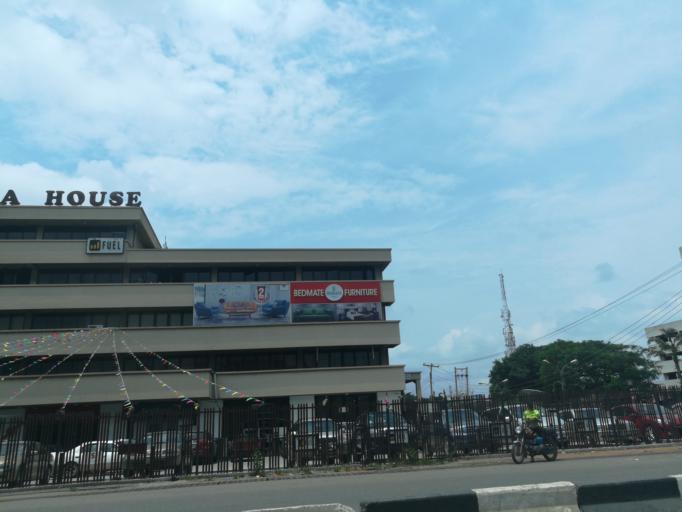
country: NG
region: Lagos
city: Ikeja
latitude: 6.5915
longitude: 3.3596
